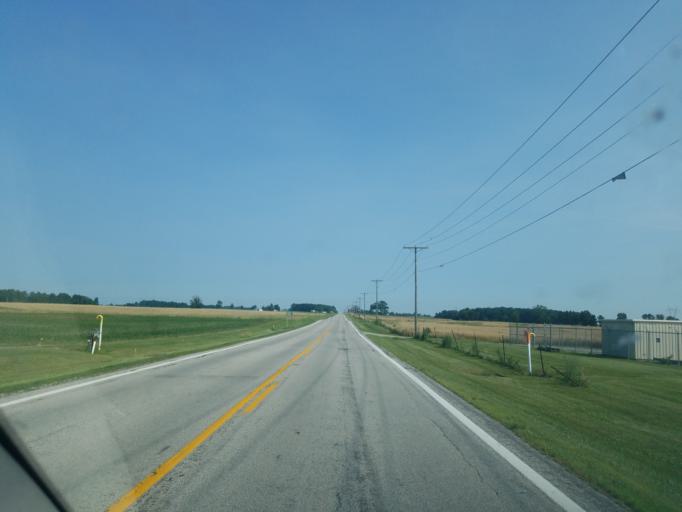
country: US
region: Ohio
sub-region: Wyandot County
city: Carey
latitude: 41.0257
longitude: -83.2954
